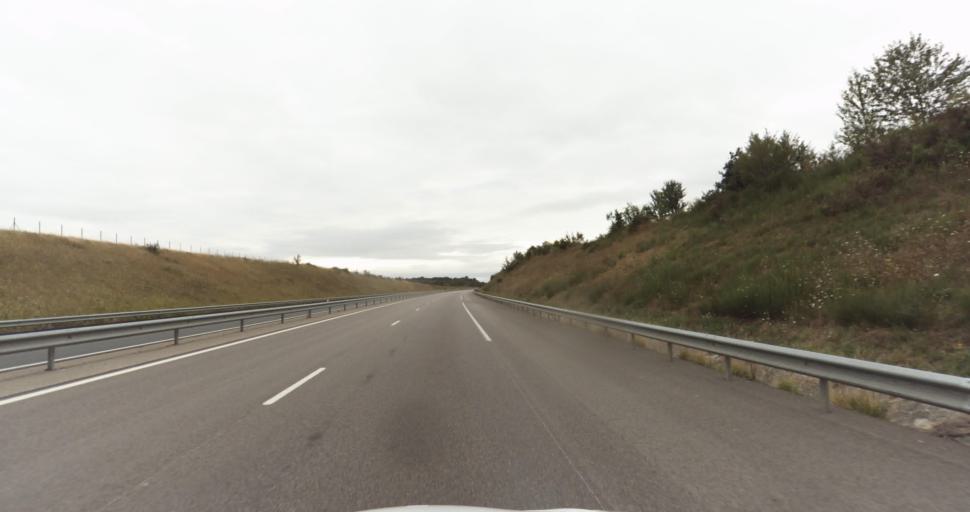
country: FR
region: Haute-Normandie
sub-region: Departement de l'Eure
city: Evreux
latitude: 48.9177
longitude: 1.1963
